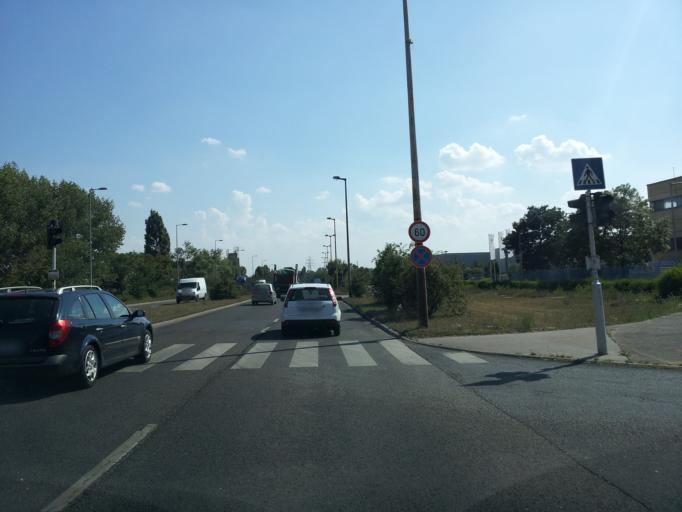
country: HU
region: Budapest
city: Budapest XXII. keruelet
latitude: 47.4505
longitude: 19.0446
